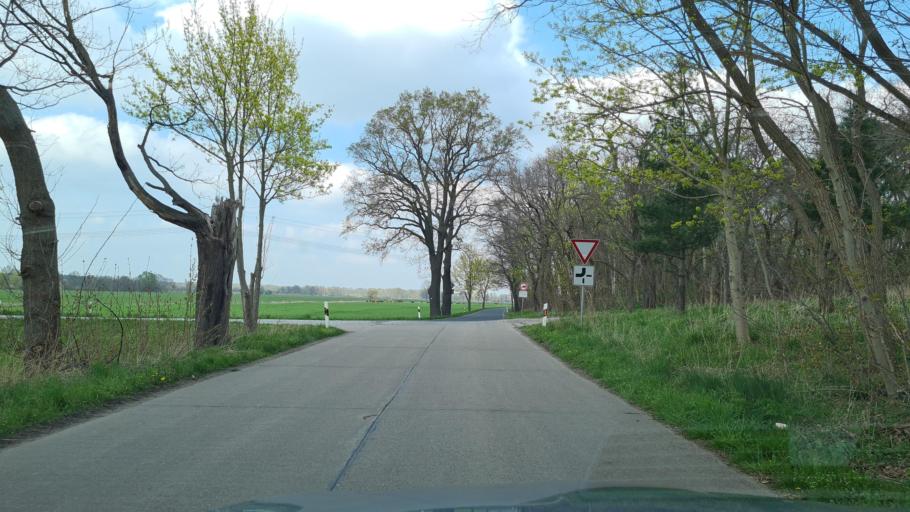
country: DE
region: Saxony
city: Wulknitz
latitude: 51.3678
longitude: 13.4193
